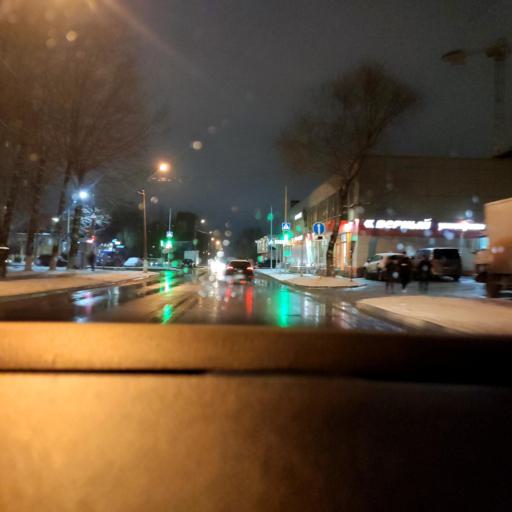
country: RU
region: Moskovskaya
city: Reutov
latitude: 55.7670
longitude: 37.8643
